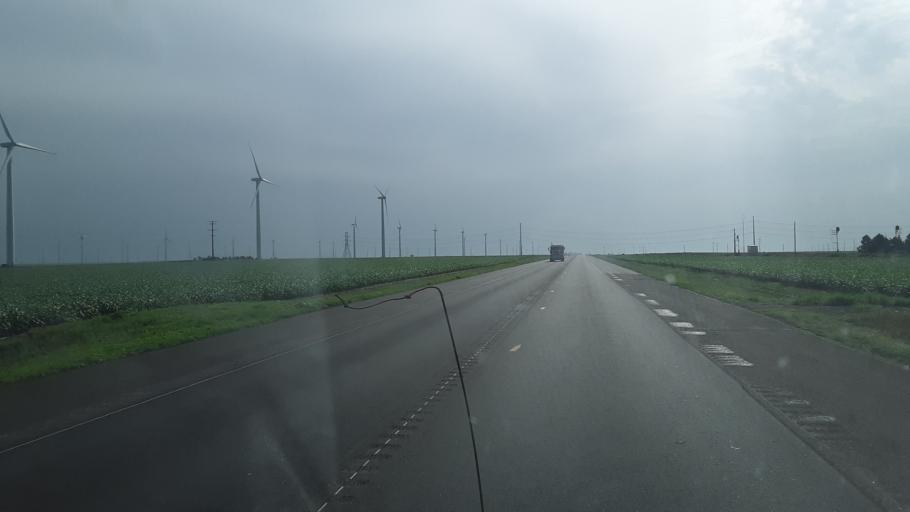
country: US
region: Kansas
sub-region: Hodgeman County
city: Jetmore
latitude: 37.8567
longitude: -99.7474
